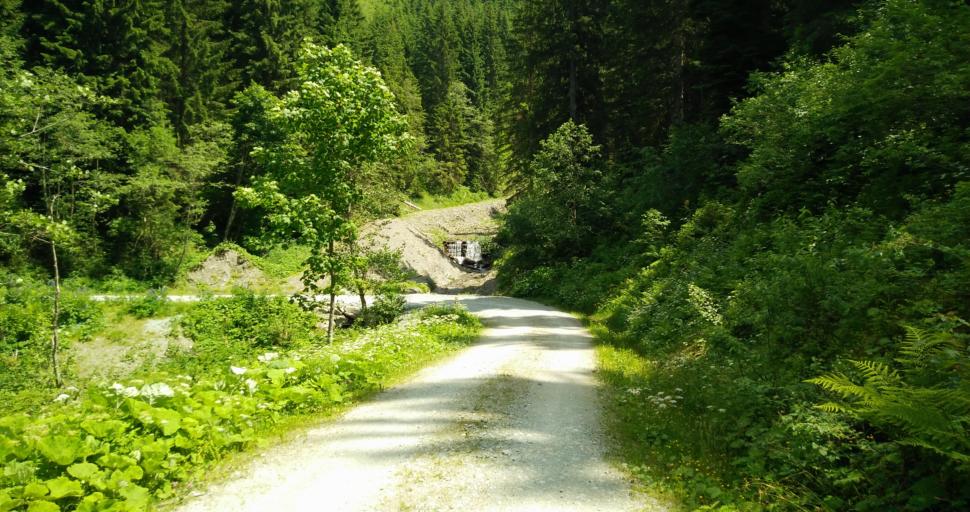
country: AT
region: Salzburg
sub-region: Politischer Bezirk Sankt Johann im Pongau
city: Huttau
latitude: 47.3938
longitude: 13.2602
